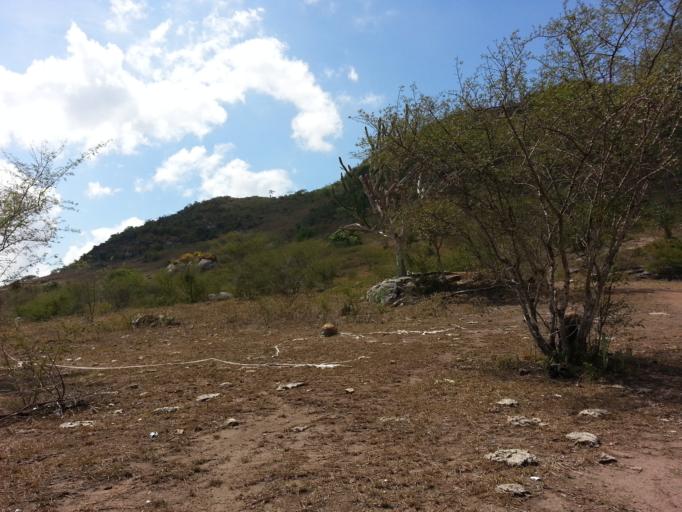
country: BR
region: Bahia
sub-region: Cruz Das Almas
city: Cruz das Almas
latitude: -12.5962
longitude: -39.1926
